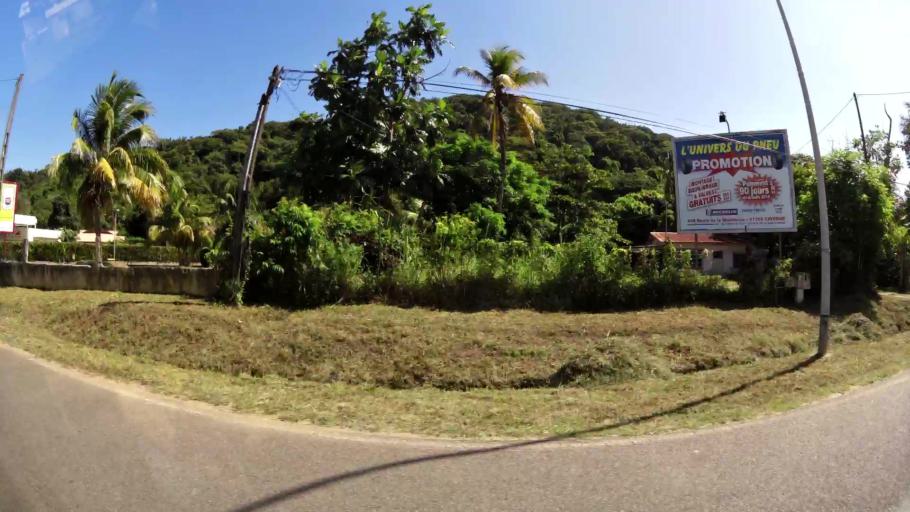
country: GF
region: Guyane
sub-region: Guyane
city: Remire-Montjoly
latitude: 4.9230
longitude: -52.2824
